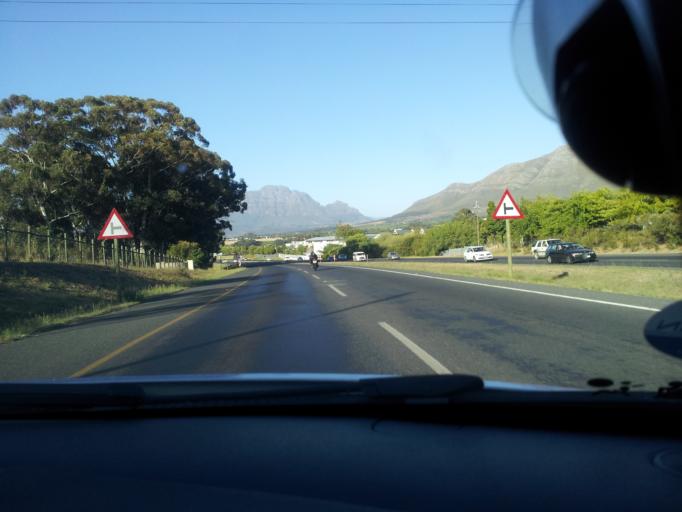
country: ZA
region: Western Cape
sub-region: Cape Winelands District Municipality
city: Stellenbosch
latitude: -33.9818
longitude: 18.8380
